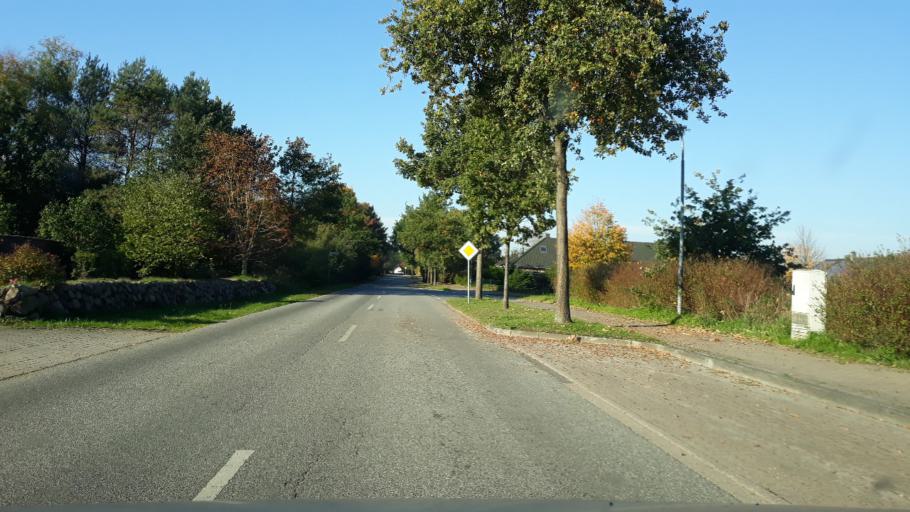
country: DE
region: Schleswig-Holstein
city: Kropp
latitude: 54.4160
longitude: 9.5264
